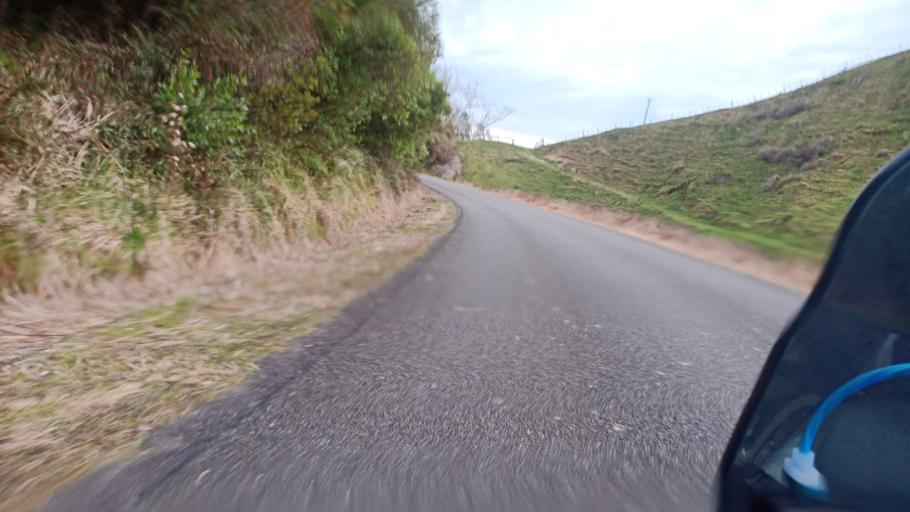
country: NZ
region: Hawke's Bay
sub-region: Wairoa District
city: Wairoa
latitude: -38.7720
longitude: 177.4262
